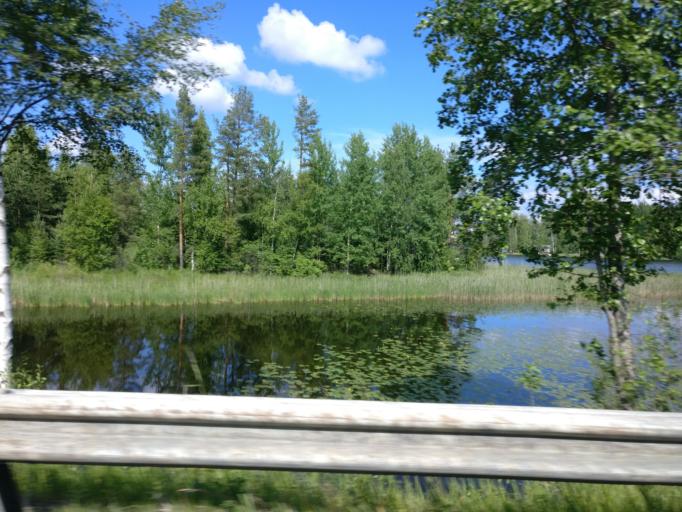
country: FI
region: Southern Savonia
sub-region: Savonlinna
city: Kerimaeki
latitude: 61.8147
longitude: 29.2624
